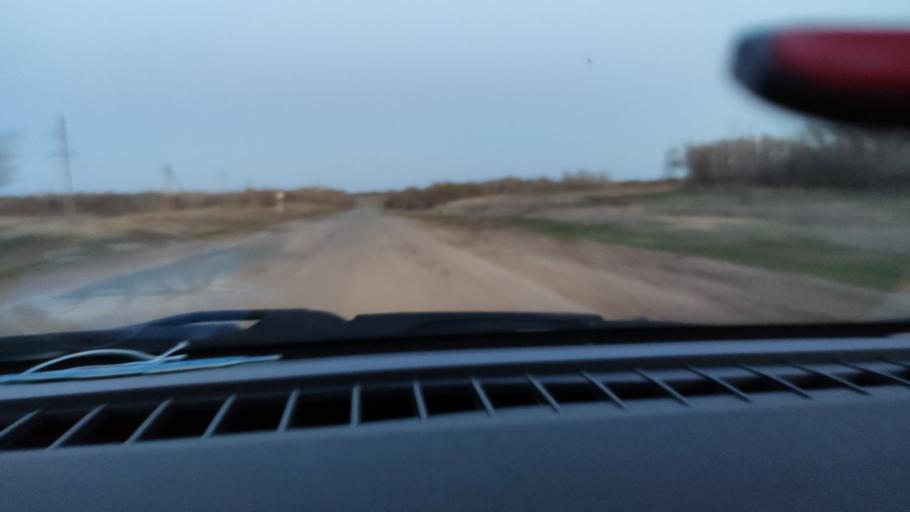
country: RU
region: Saratov
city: Rovnoye
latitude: 51.0466
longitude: 46.0514
